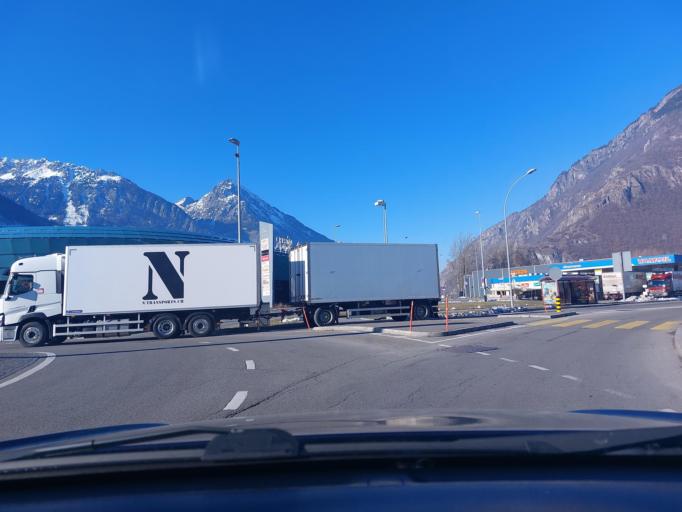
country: CH
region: Valais
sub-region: Martigny District
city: Martigny-Ville
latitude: 46.1106
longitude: 7.0767
